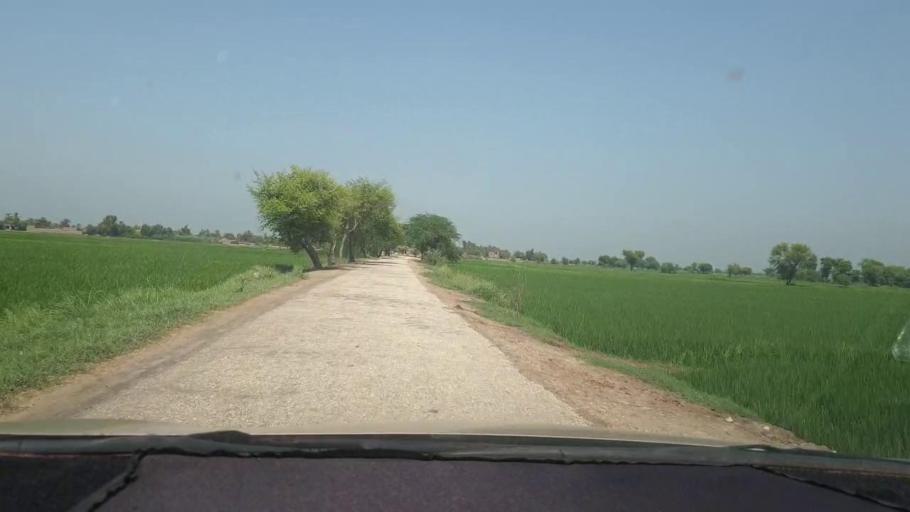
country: PK
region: Sindh
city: Kambar
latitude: 27.6196
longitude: 68.0538
